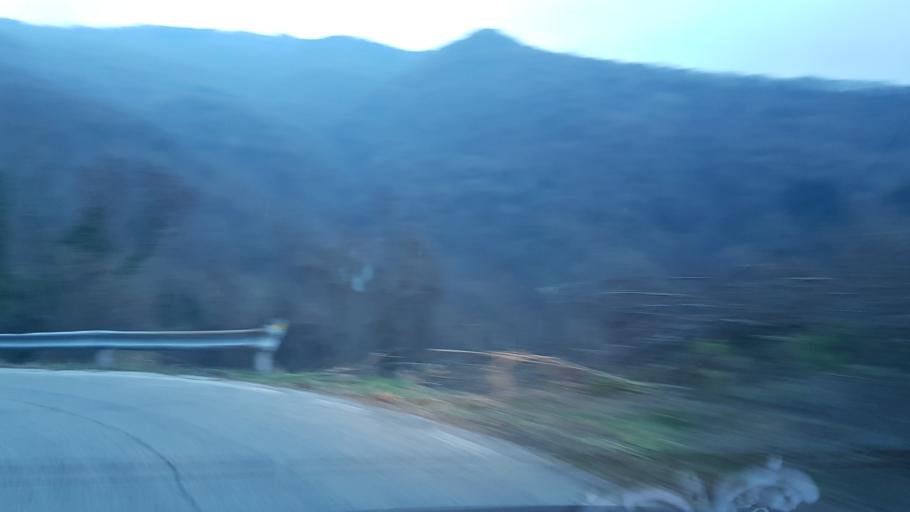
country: IT
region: Friuli Venezia Giulia
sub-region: Provincia di Udine
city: Attimis
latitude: 46.1977
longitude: 13.3427
